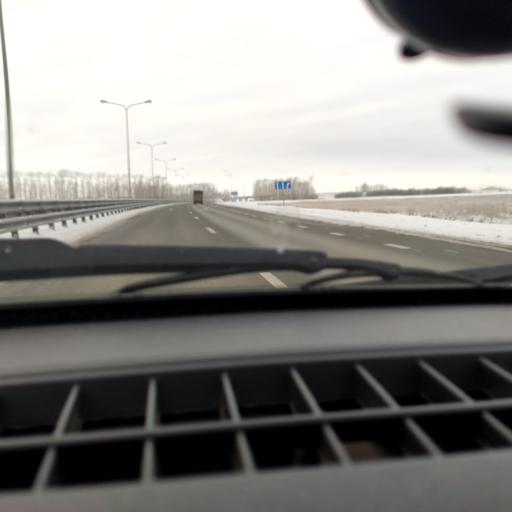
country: RU
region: Bashkortostan
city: Kushnarenkovo
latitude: 55.0651
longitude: 55.3273
